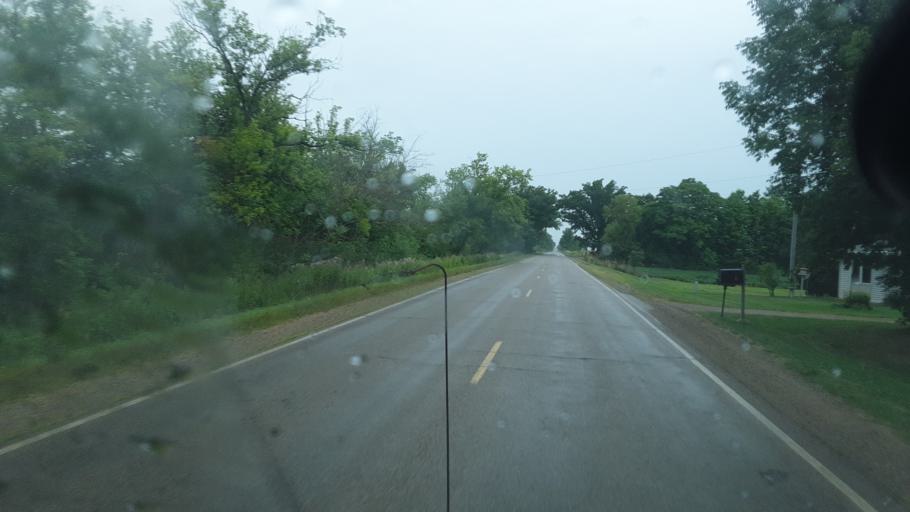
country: US
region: Michigan
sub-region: Hillsdale County
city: Reading
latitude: 41.7081
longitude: -84.7549
